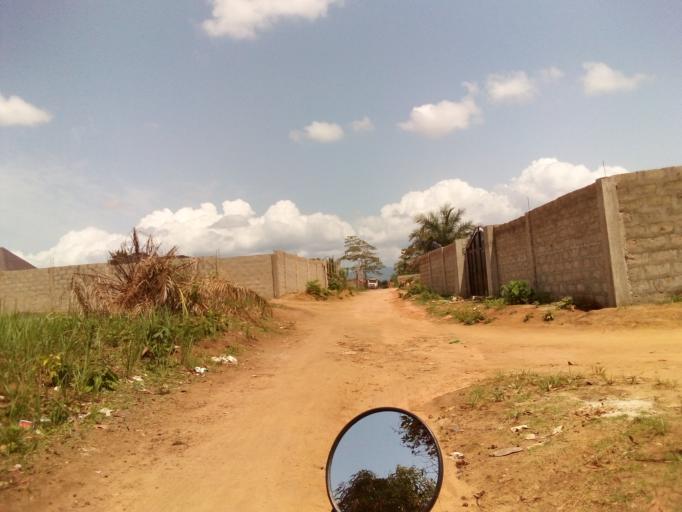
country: SL
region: Western Area
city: Waterloo
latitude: 8.3371
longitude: -13.0230
